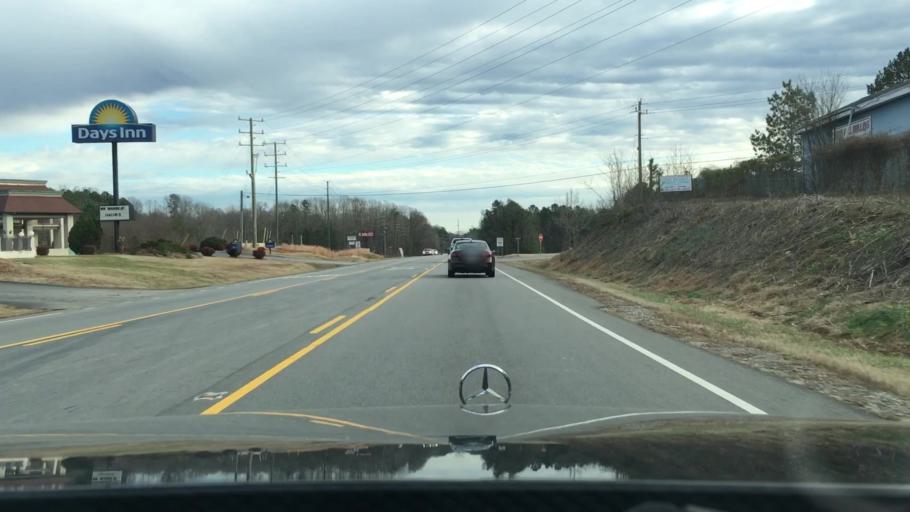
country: US
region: North Carolina
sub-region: Caswell County
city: Yanceyville
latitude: 36.4160
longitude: -79.3479
